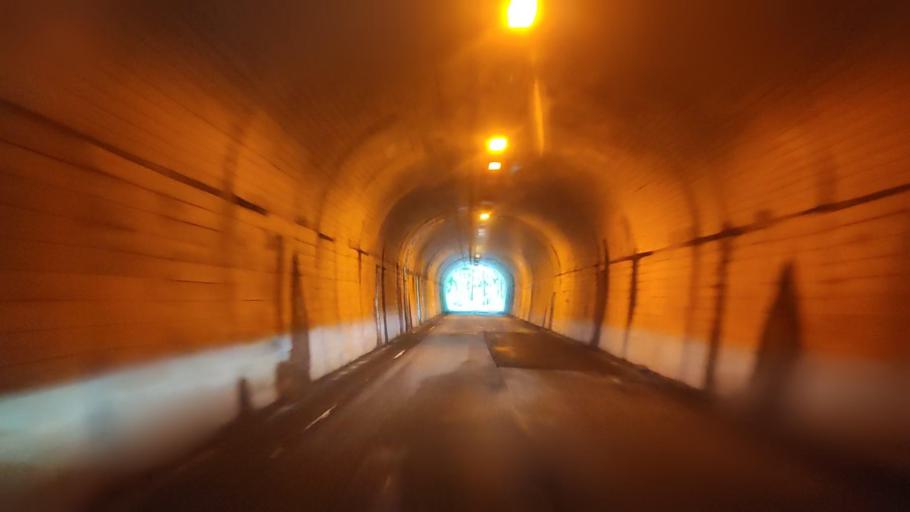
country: JP
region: Nara
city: Yoshino-cho
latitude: 34.3974
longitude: 135.9224
